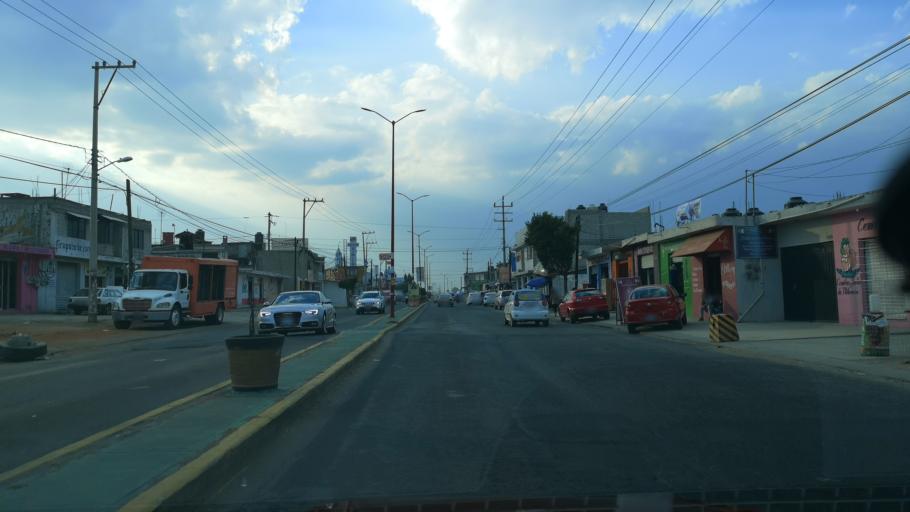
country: MX
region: Puebla
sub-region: Juan C. Bonilla
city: Santa Maria Zacatepec
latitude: 19.1204
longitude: -98.3631
